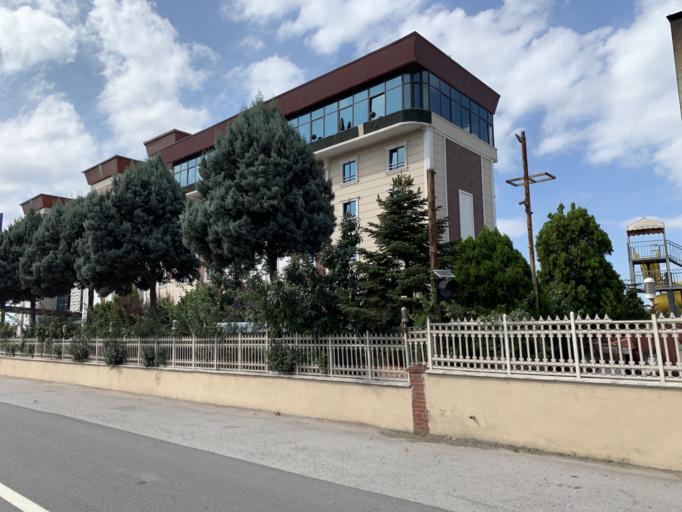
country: TR
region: Yalova
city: Taskopru
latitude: 40.6873
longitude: 29.4455
